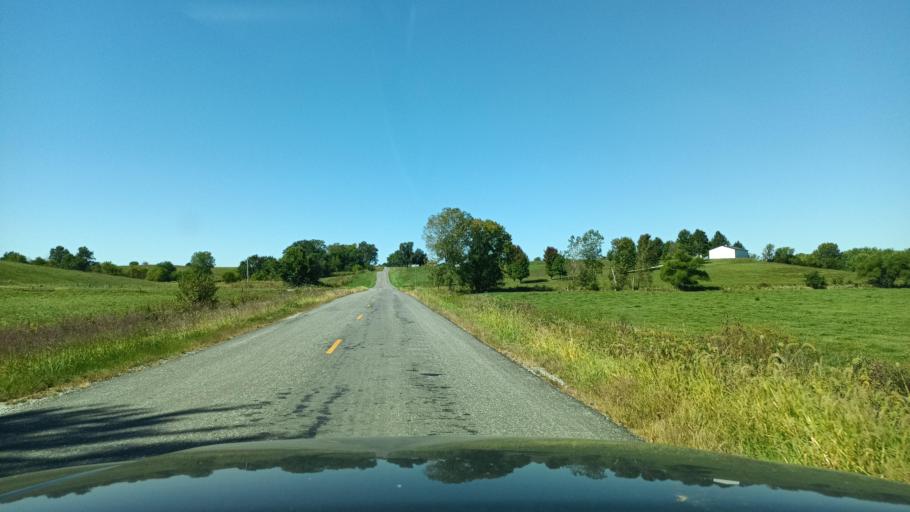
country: US
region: Missouri
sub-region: Adair County
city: Kirksville
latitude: 40.3299
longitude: -92.5517
